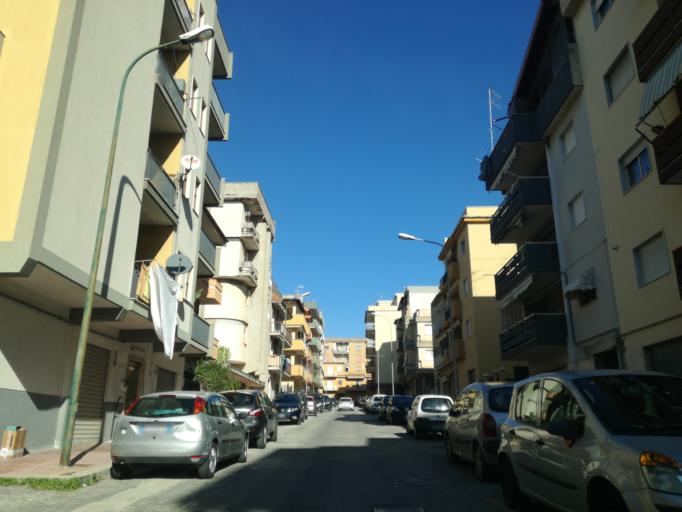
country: IT
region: Sicily
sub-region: Provincia di Caltanissetta
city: Gela
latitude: 37.0717
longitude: 14.2321
